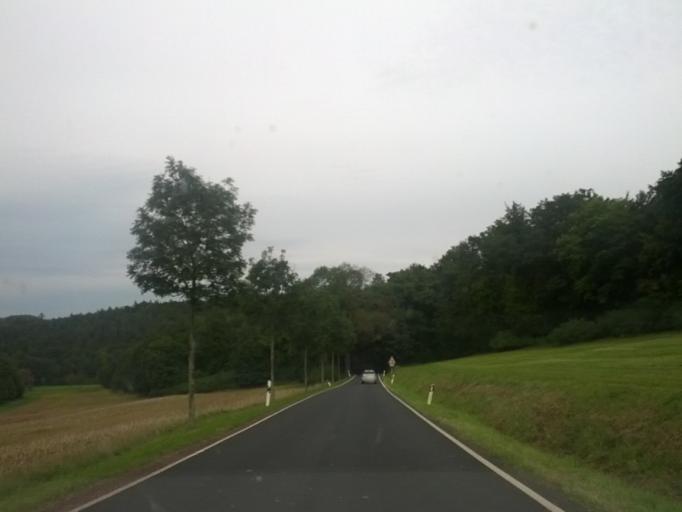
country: DE
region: Thuringia
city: Wolfsburg-Unkeroda
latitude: 50.9212
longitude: 10.2839
